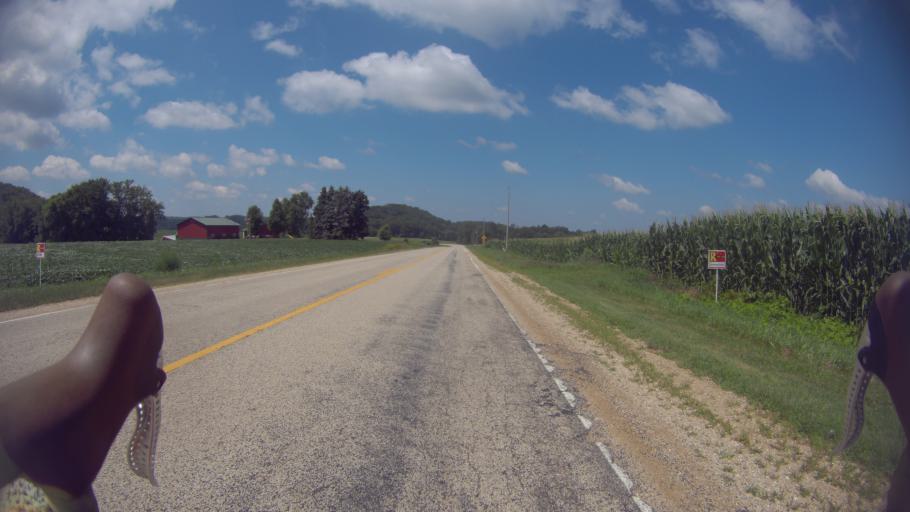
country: US
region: Wisconsin
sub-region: Sauk County
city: Sauk City
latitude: 43.2456
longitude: -89.6274
